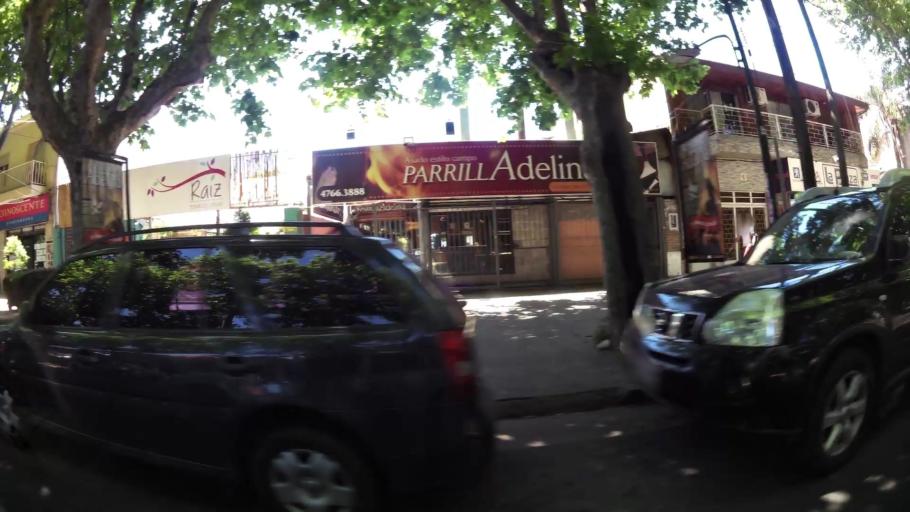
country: AR
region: Buenos Aires
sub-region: Partido de General San Martin
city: General San Martin
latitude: -34.5189
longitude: -58.5440
